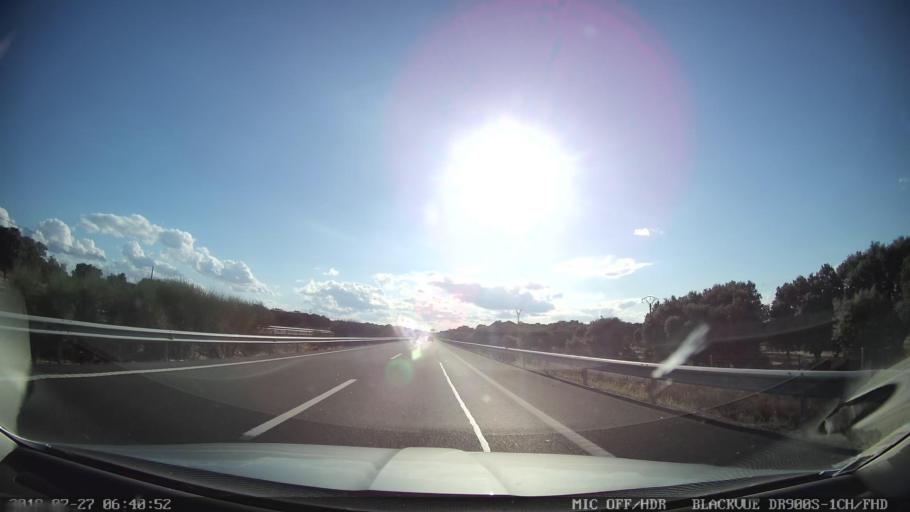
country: ES
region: Extremadura
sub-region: Provincia de Caceres
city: Peraleda de la Mata
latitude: 39.8896
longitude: -5.4519
